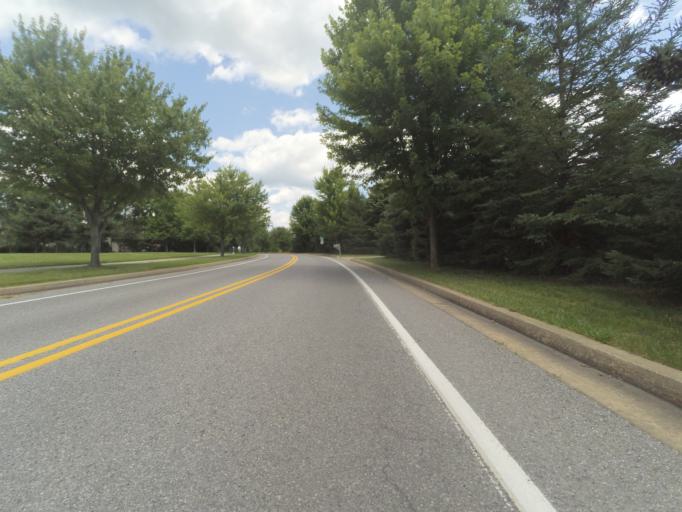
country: US
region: Pennsylvania
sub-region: Centre County
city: Lemont
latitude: 40.7885
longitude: -77.8177
